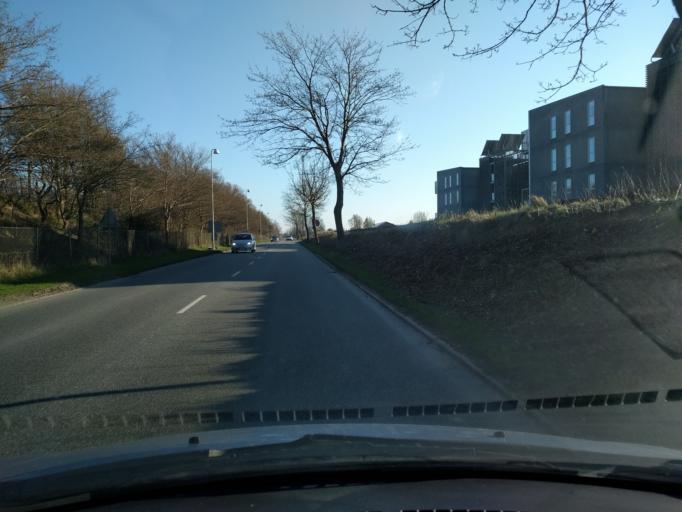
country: DK
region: Capital Region
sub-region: Hillerod Kommune
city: Hillerod
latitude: 55.9409
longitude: 12.2642
